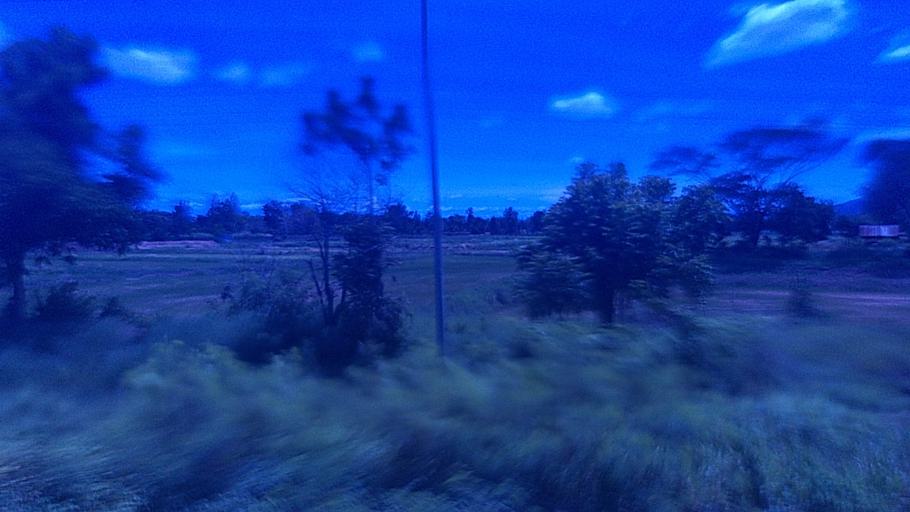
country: TH
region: Chaiyaphum
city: Phu Khiao
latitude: 16.3272
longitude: 102.2143
